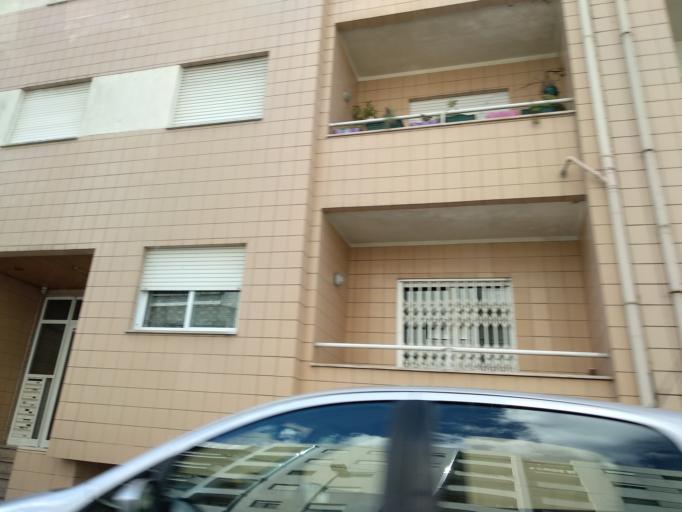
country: PT
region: Braga
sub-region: Braga
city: Braga
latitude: 41.5620
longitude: -8.4059
